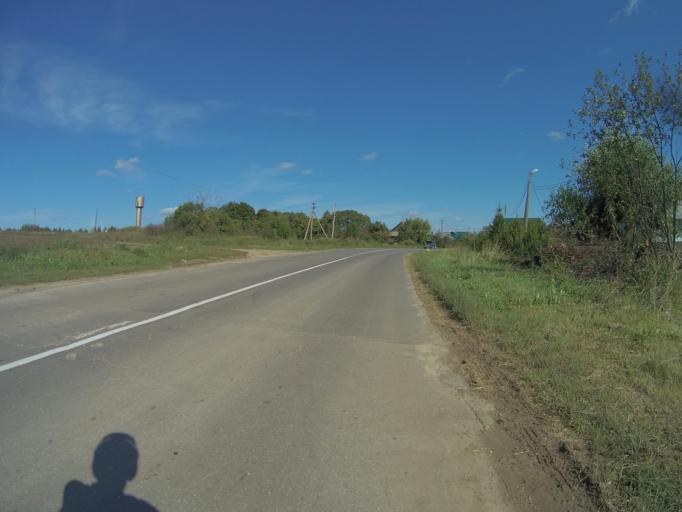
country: RU
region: Vladimir
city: Bogolyubovo
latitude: 56.2967
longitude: 40.5585
